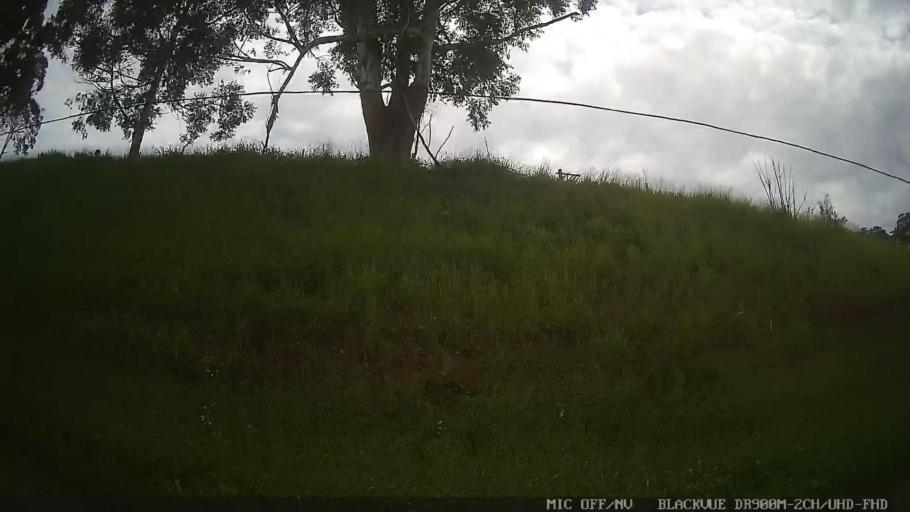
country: BR
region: Sao Paulo
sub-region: Rio Grande Da Serra
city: Rio Grande da Serra
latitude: -23.6995
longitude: -46.2679
